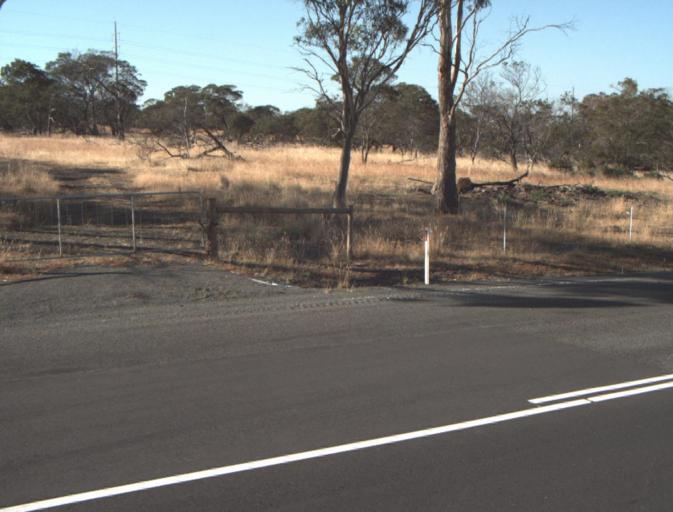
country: AU
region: Tasmania
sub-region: Launceston
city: Newstead
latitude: -41.4448
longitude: 147.2311
